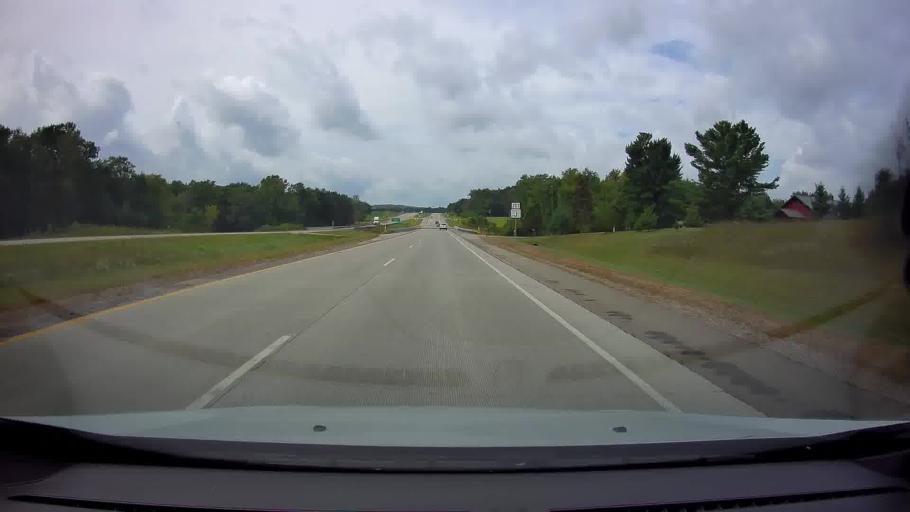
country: US
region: Wisconsin
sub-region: Shawano County
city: Wittenberg
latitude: 44.8039
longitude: -89.0145
